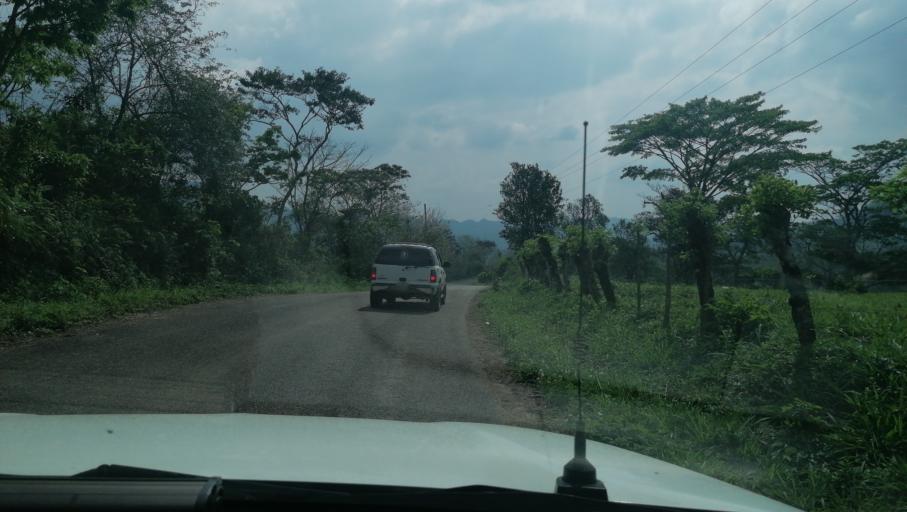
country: MX
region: Chiapas
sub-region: Francisco Leon
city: San Miguel la Sardina
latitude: 17.2310
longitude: -93.3437
